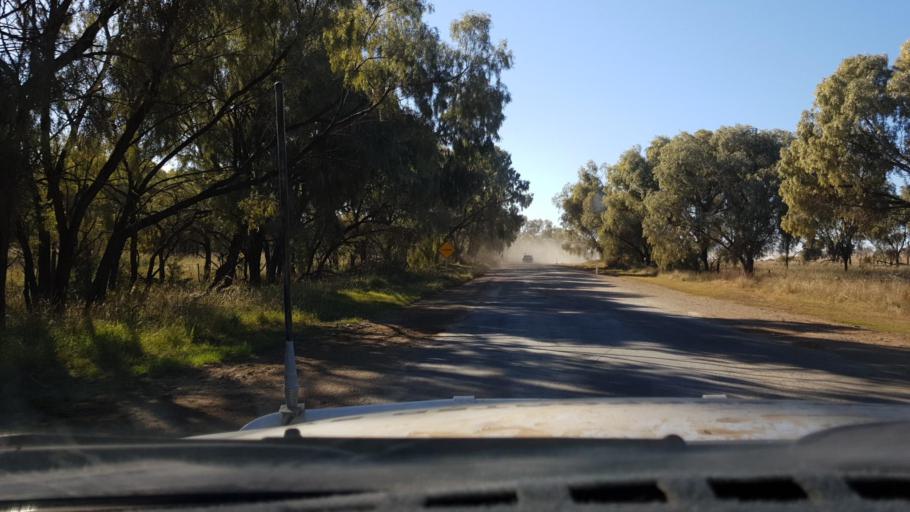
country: AU
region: New South Wales
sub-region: Narrabri
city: Blair Athol
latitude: -30.6753
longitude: 150.4318
